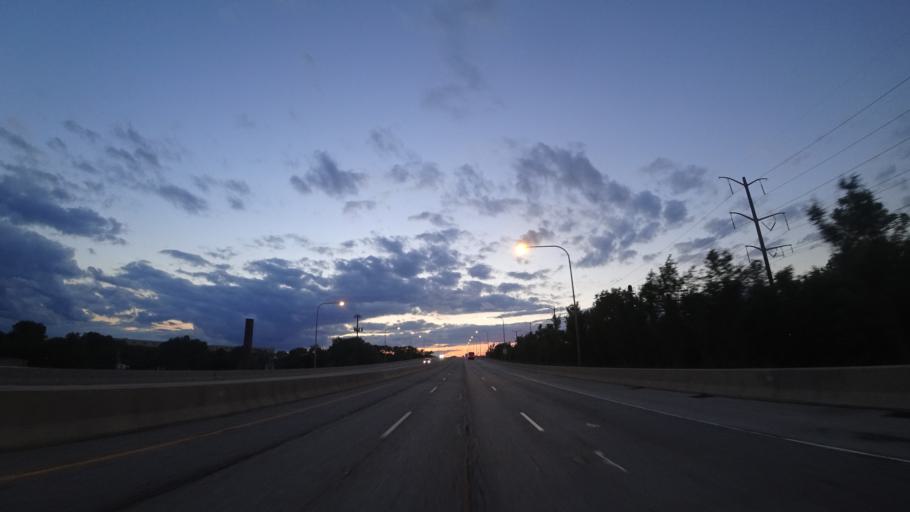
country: US
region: Illinois
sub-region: Cook County
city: Chicago
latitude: 41.7537
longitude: -87.5911
